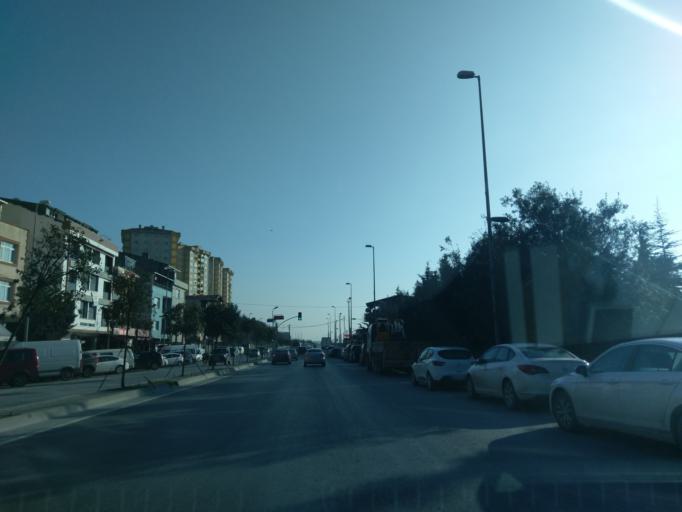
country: TR
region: Istanbul
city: Mahmutbey
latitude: 41.0303
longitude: 28.7680
